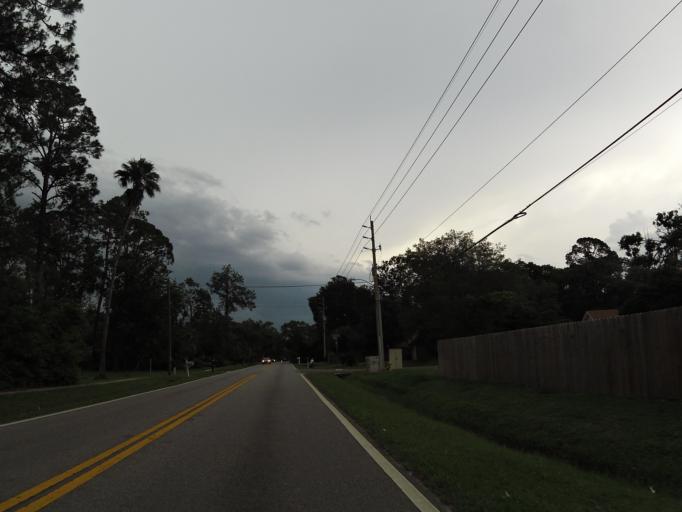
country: US
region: Florida
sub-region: Duval County
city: Jacksonville
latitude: 30.2797
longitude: -81.5852
